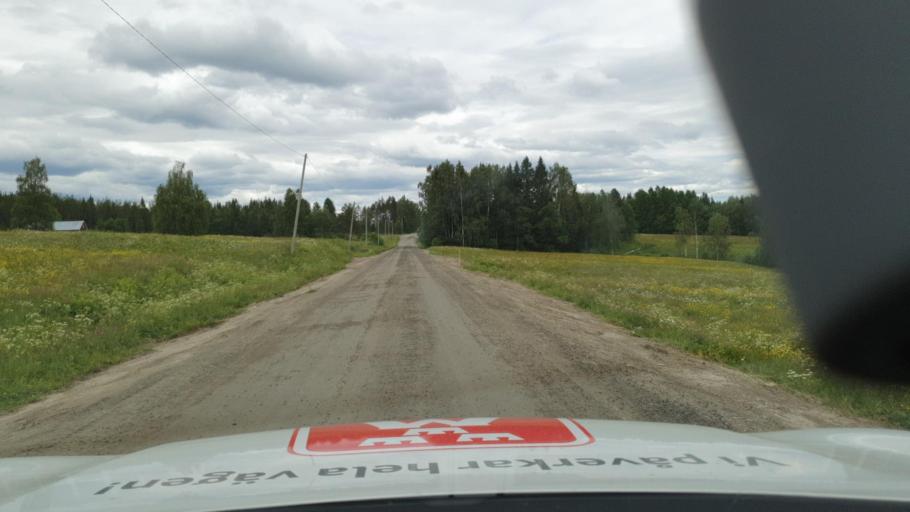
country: SE
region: Vaesterbotten
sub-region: Nordmalings Kommun
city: Nordmaling
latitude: 63.7150
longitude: 19.4280
